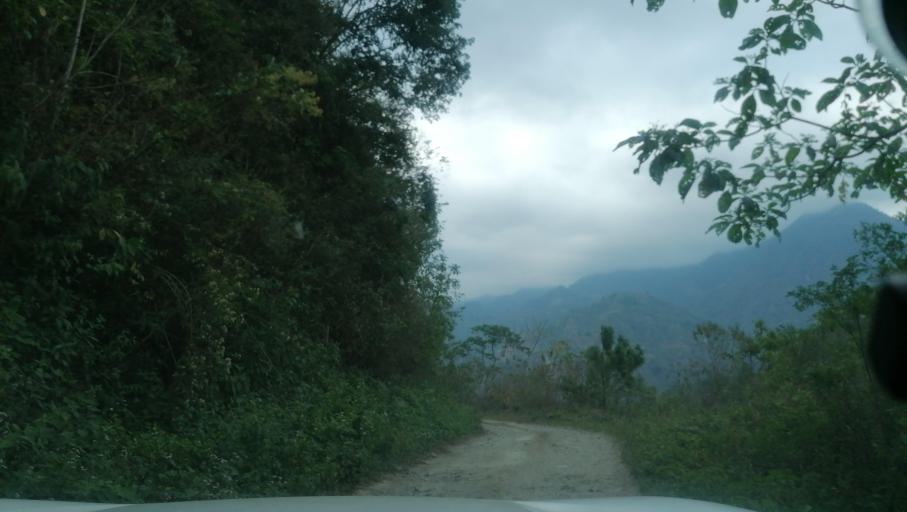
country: MX
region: Chiapas
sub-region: Cacahoatan
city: Benito Juarez
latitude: 15.1657
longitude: -92.1665
